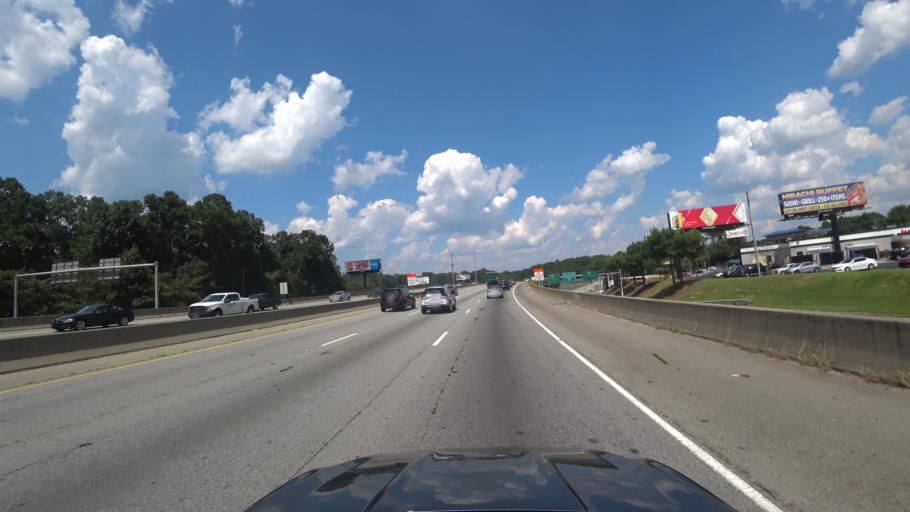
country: US
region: Georgia
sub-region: DeKalb County
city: Doraville
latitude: 33.9209
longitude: -84.2832
